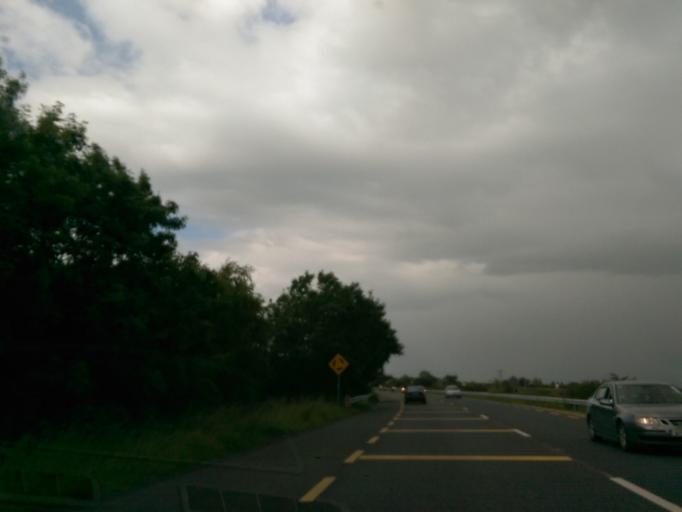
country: IE
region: Connaught
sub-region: County Galway
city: Oranmore
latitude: 53.2681
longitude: -8.9198
